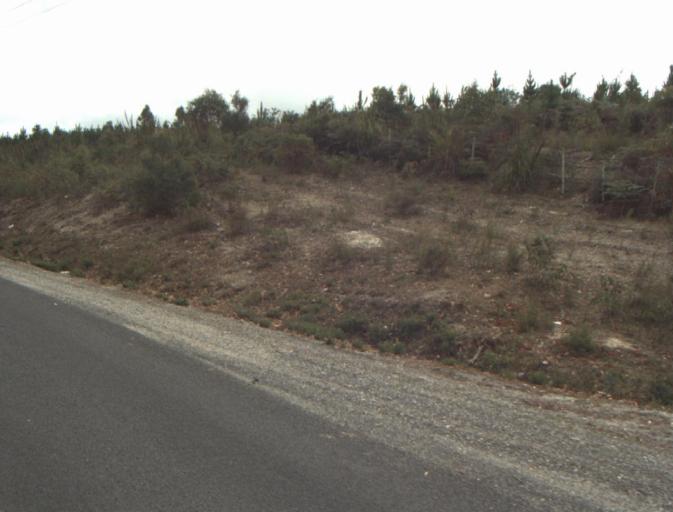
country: AU
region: Tasmania
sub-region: Dorset
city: Bridport
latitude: -41.1685
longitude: 147.2626
